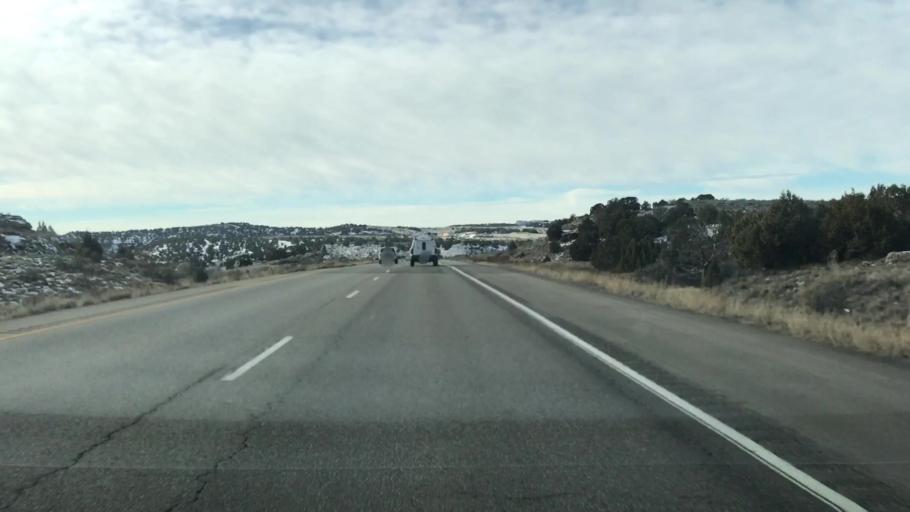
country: US
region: Colorado
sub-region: Garfield County
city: Parachute
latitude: 39.3736
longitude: -108.1655
